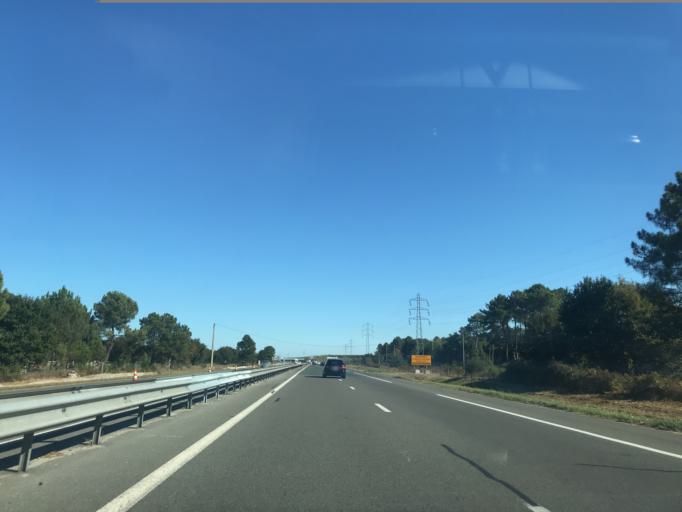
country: FR
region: Aquitaine
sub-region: Departement de la Gironde
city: Le Teich
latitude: 44.6130
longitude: -1.0385
